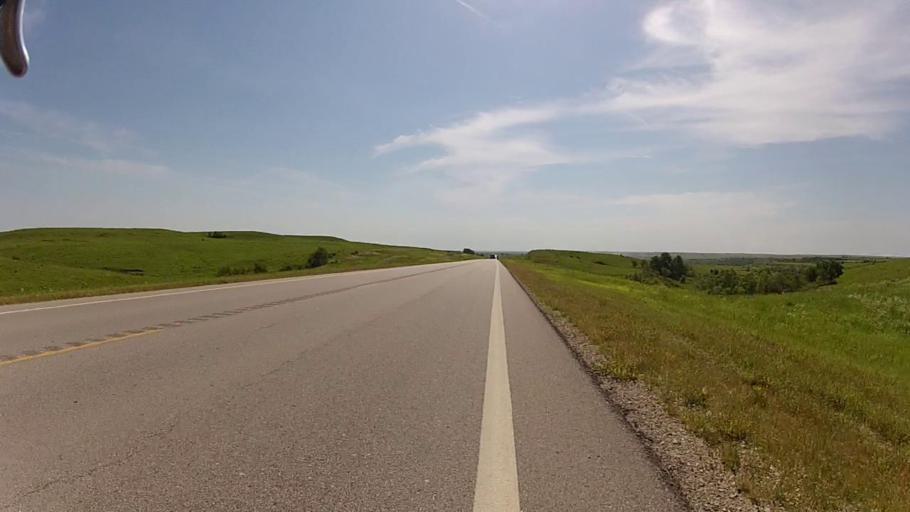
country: US
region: Kansas
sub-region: Cowley County
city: Winfield
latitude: 37.1107
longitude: -96.6397
